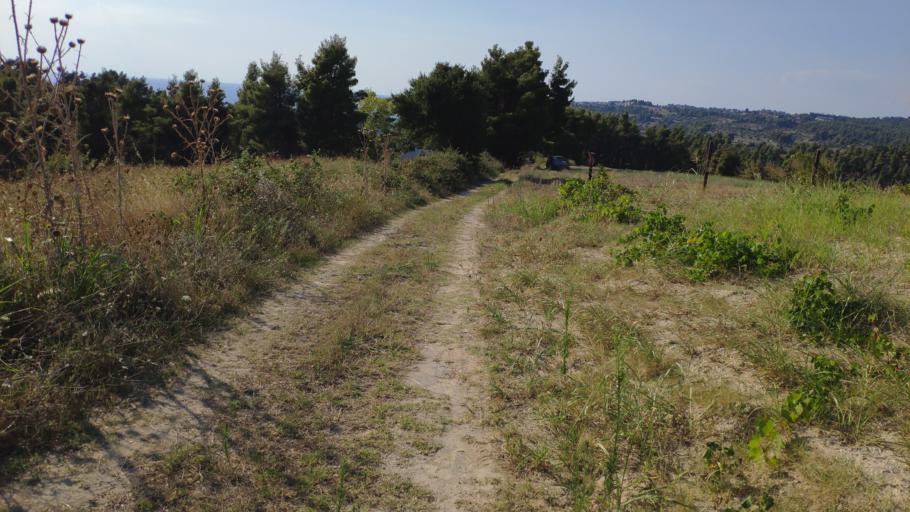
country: GR
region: Central Macedonia
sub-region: Nomos Chalkidikis
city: Kassandreia
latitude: 40.0294
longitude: 23.3683
